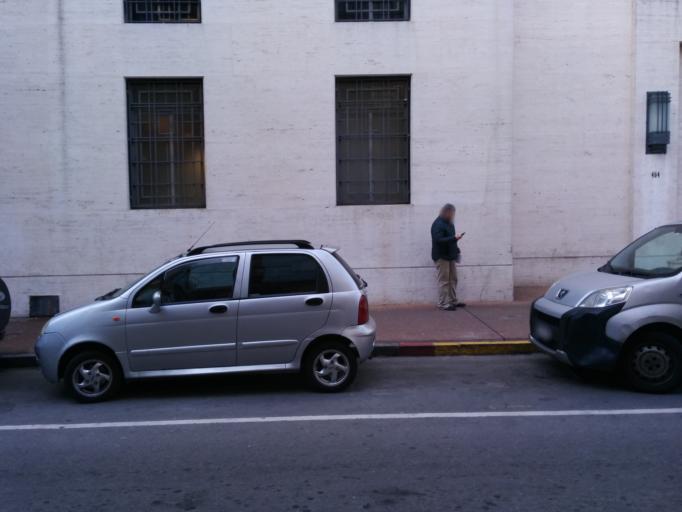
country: UY
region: Montevideo
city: Montevideo
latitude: -34.9069
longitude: -56.2061
